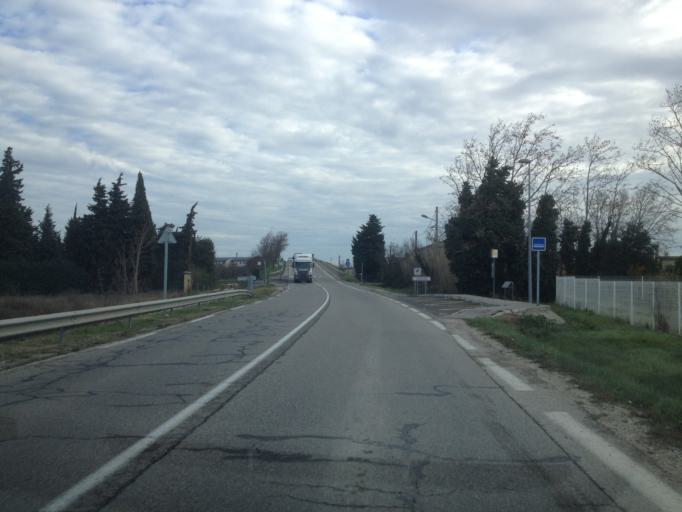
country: FR
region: Provence-Alpes-Cote d'Azur
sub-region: Departement du Vaucluse
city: Sorgues
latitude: 43.9919
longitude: 4.8671
